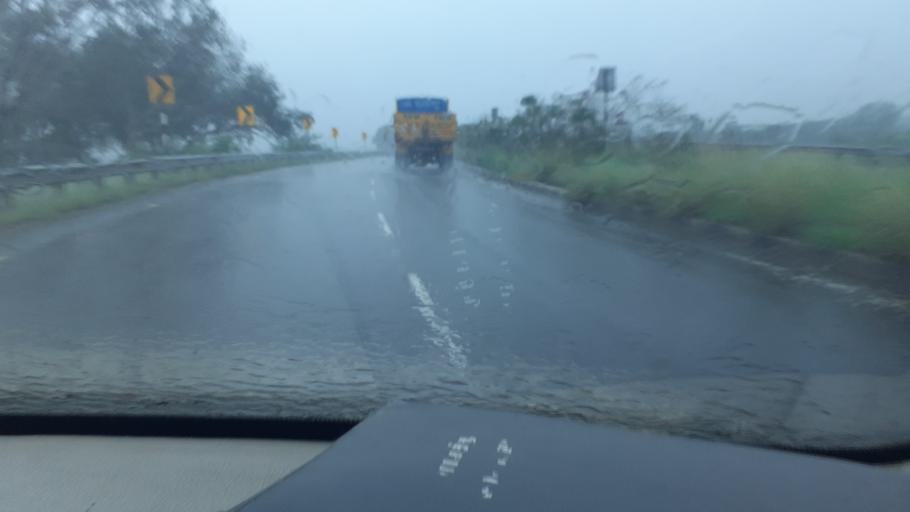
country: IN
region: Tamil Nadu
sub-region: Virudhunagar
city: Sattur
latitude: 9.4384
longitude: 77.9235
